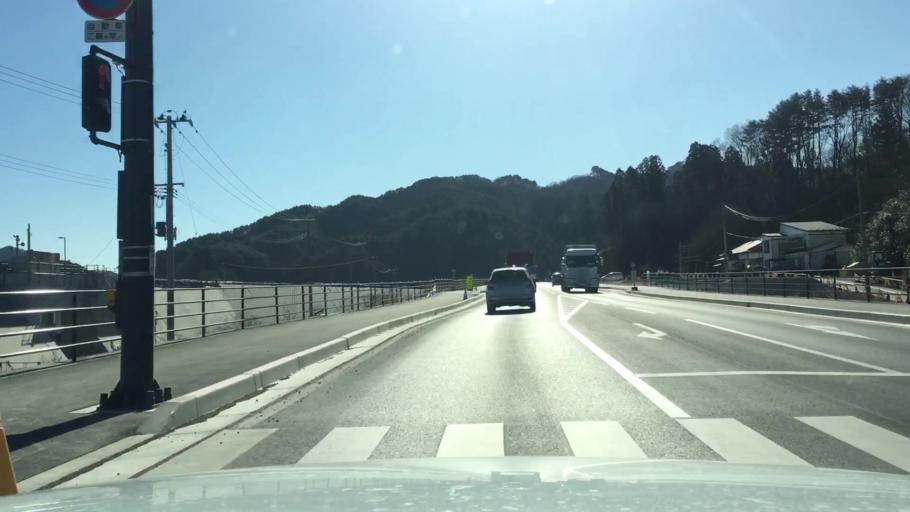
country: JP
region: Iwate
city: Yamada
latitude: 39.4535
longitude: 141.9609
